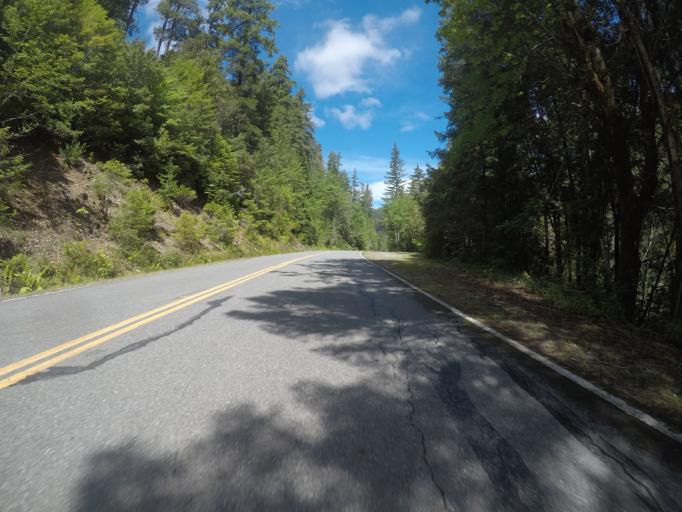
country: US
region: California
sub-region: Del Norte County
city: Bertsch-Oceanview
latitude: 41.7242
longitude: -123.9545
